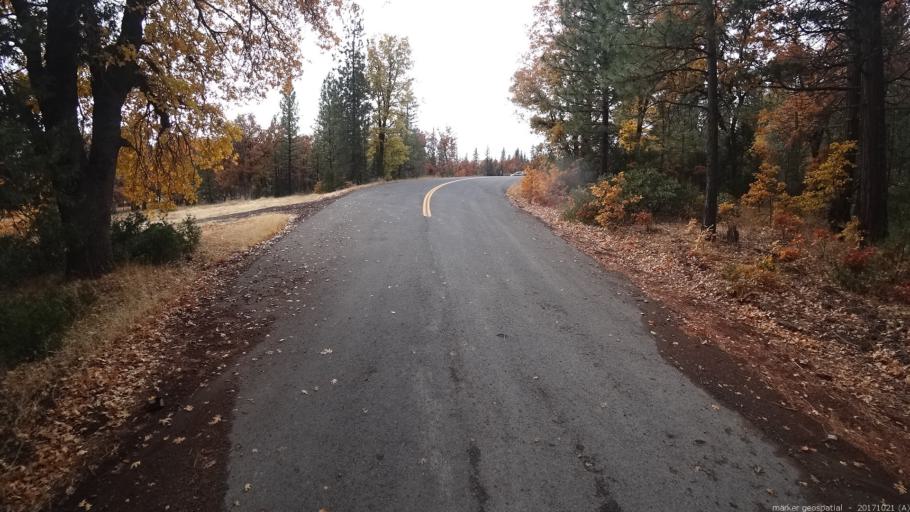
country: US
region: California
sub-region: Shasta County
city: Burney
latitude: 41.0514
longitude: -121.6374
